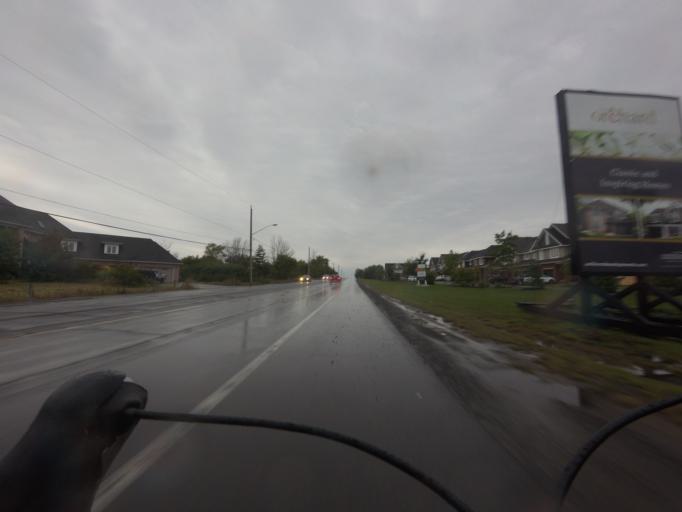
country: CA
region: Ontario
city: Bells Corners
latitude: 45.2500
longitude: -75.7173
